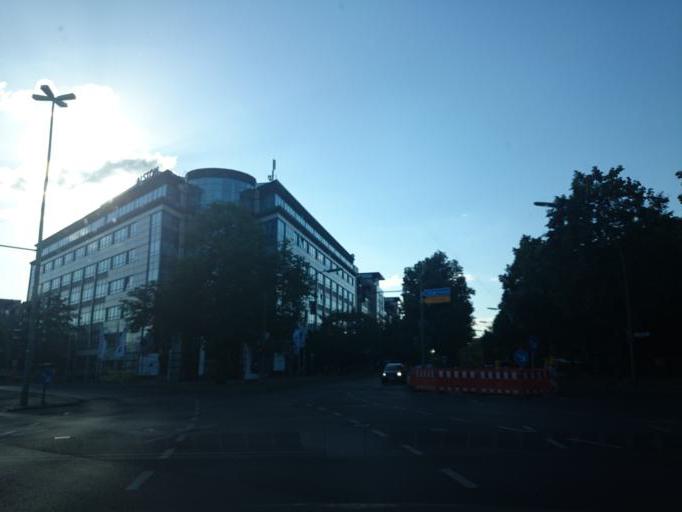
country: DE
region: Berlin
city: Britz
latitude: 52.4525
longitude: 13.4331
